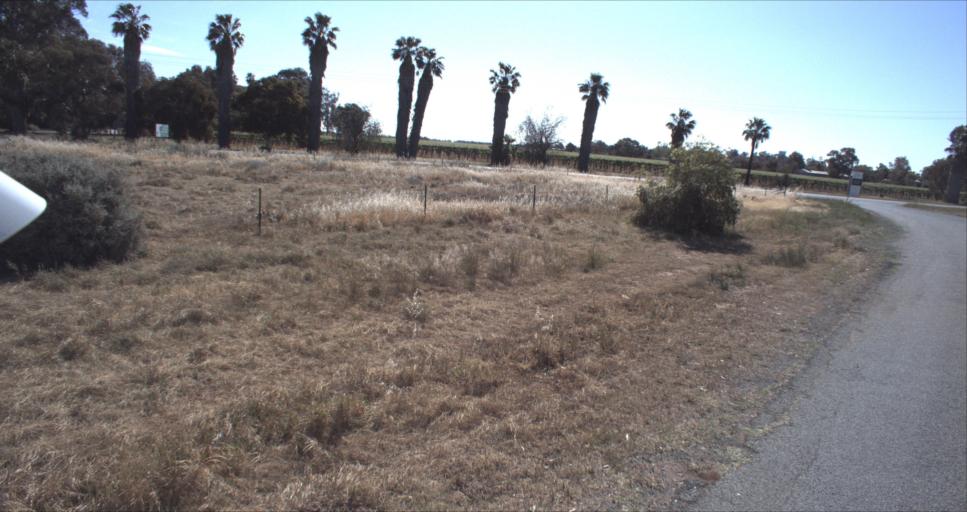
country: AU
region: New South Wales
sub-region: Leeton
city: Leeton
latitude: -34.5567
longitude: 146.3849
